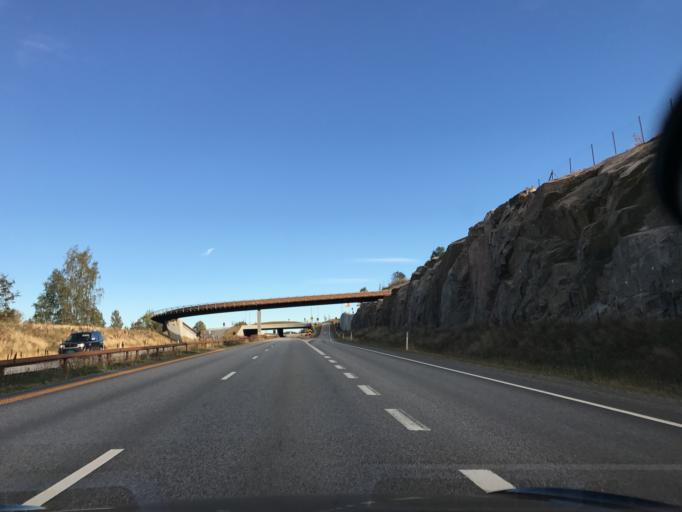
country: NO
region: Hedmark
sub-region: Stange
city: Stange
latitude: 60.5599
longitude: 11.2539
